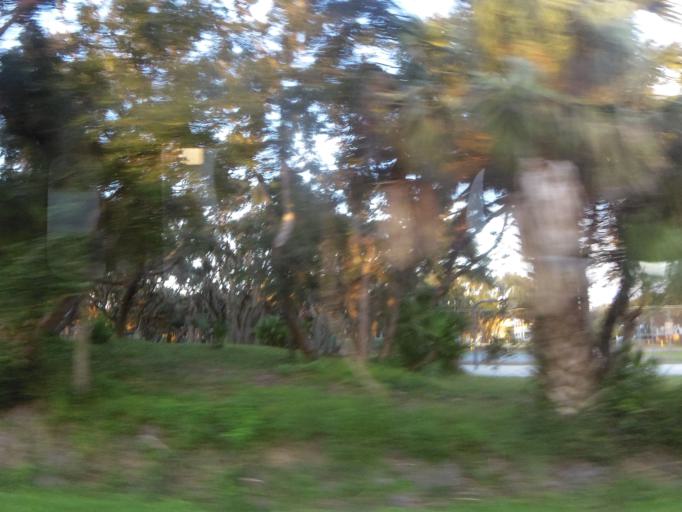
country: US
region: Florida
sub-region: Saint Johns County
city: Villano Beach
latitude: 29.9243
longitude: -81.2974
